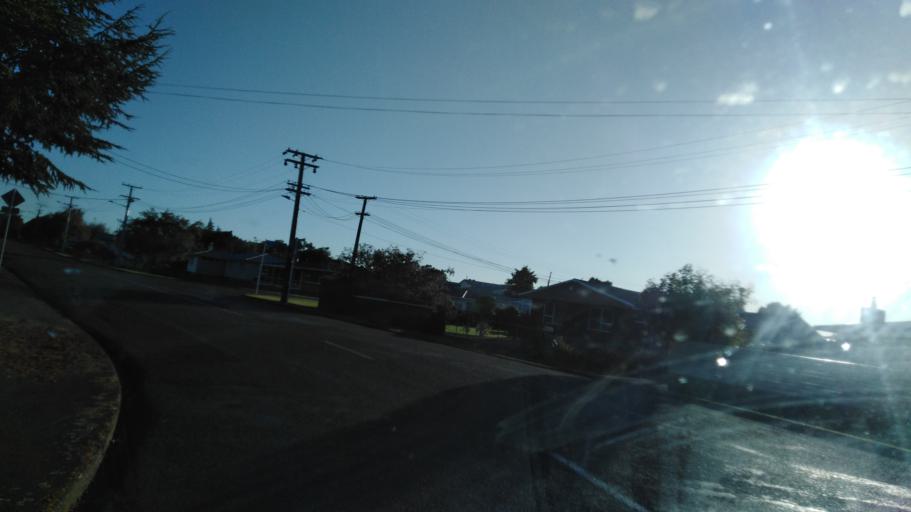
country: NZ
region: Manawatu-Wanganui
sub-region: Rangitikei District
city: Bulls
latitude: -40.0706
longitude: 175.3823
